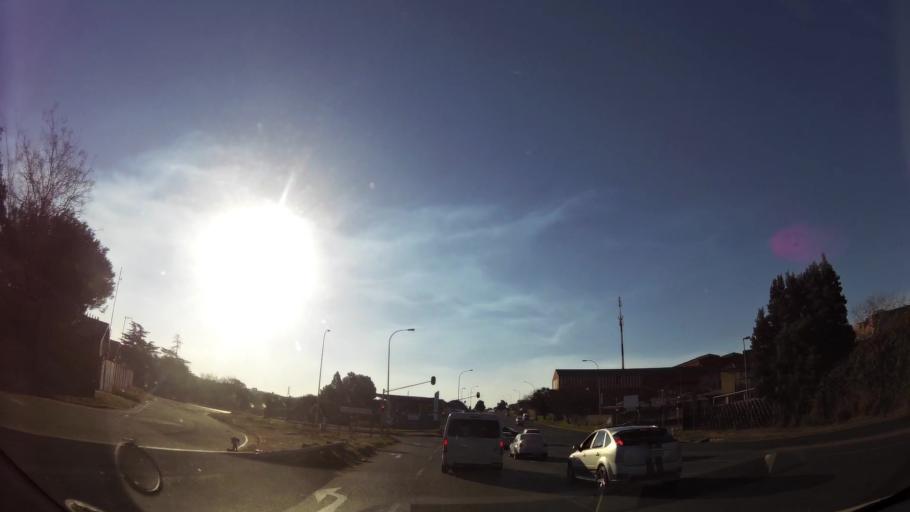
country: ZA
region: Gauteng
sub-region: City of Johannesburg Metropolitan Municipality
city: Roodepoort
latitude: -26.1512
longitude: 27.8643
